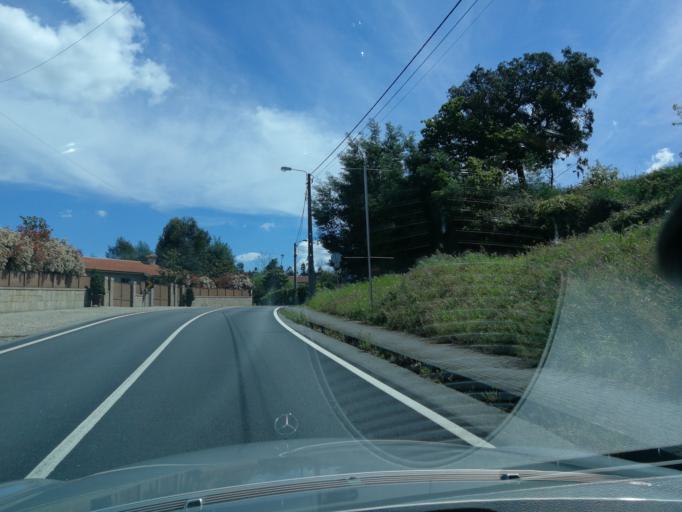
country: PT
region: Braga
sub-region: Vila Nova de Famalicao
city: Calendario
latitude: 41.4208
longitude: -8.5355
